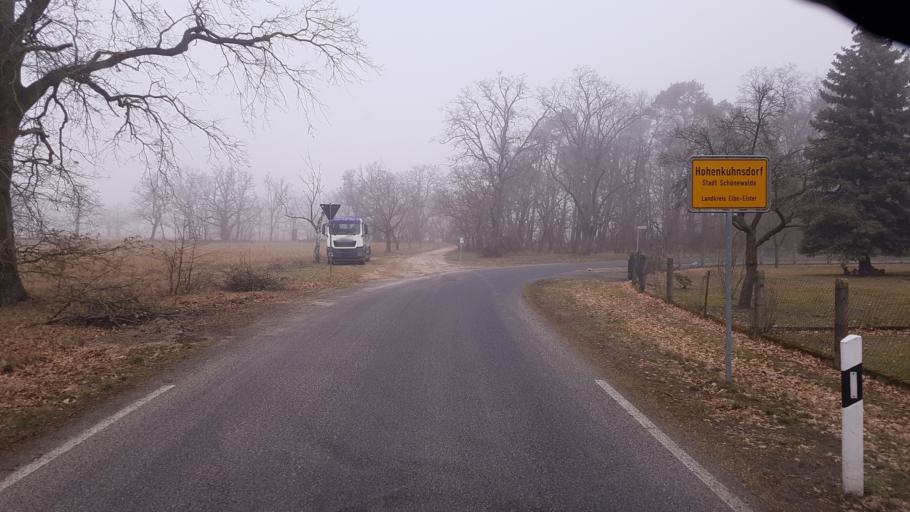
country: DE
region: Saxony-Anhalt
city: Holzdorf
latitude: 51.8610
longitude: 13.2096
